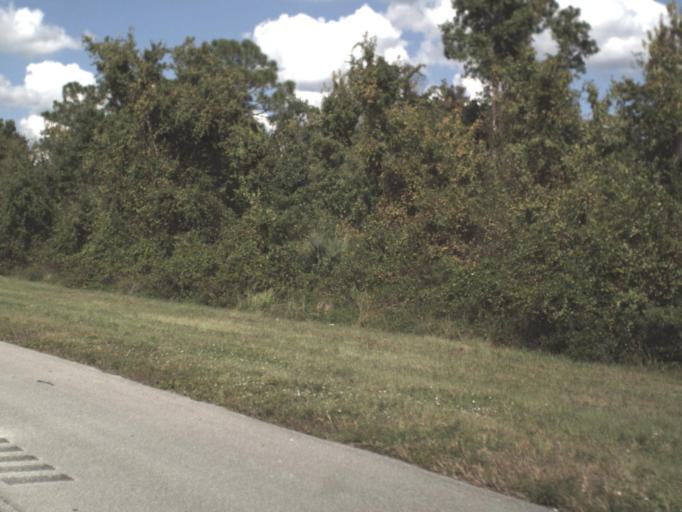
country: US
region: Florida
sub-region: Indian River County
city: Fellsmere
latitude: 27.6199
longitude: -80.8362
